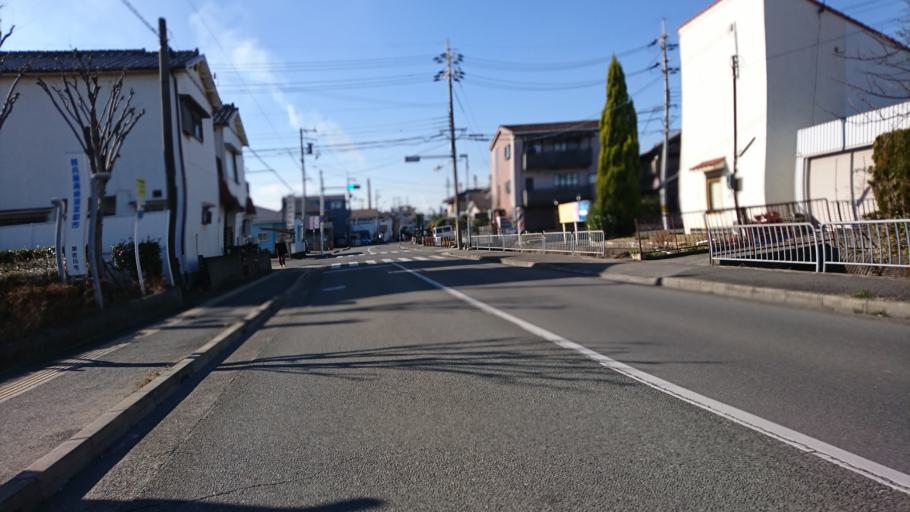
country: JP
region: Hyogo
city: Kakogawacho-honmachi
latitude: 34.7297
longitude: 134.8442
